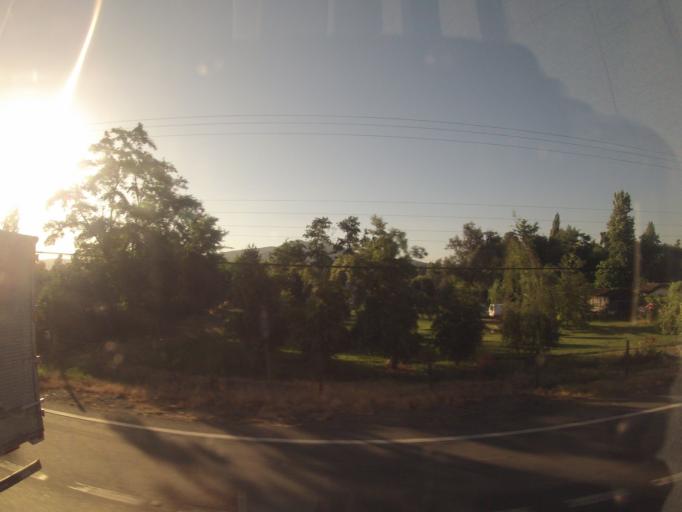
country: CL
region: O'Higgins
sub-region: Provincia de Colchagua
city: Chimbarongo
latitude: -34.6948
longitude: -71.0182
